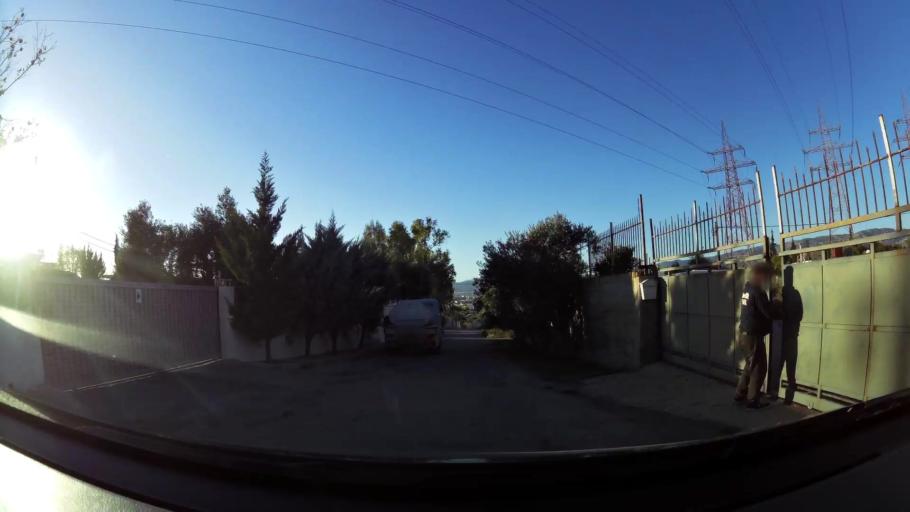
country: GR
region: Attica
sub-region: Nomarchia Athinas
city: Skaramangas
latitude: 38.0306
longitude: 23.6206
